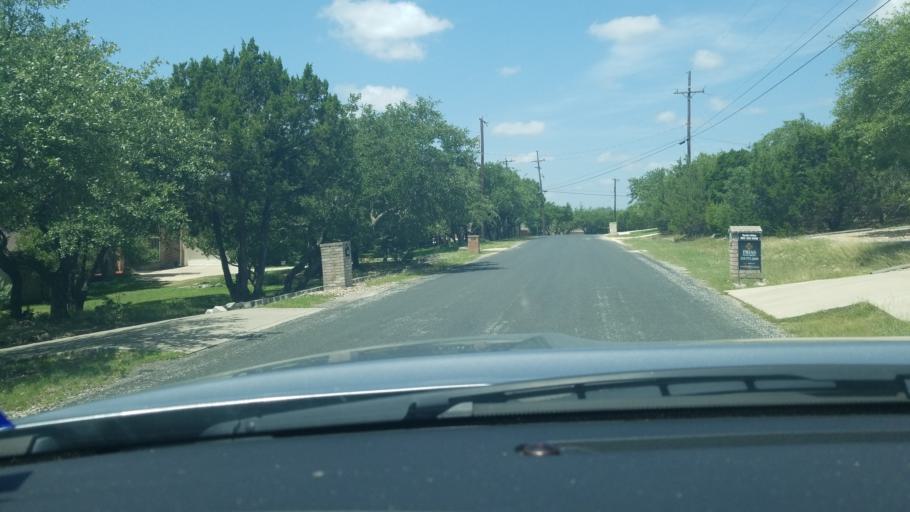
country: US
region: Texas
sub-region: Bexar County
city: Timberwood Park
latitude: 29.6916
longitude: -98.4827
